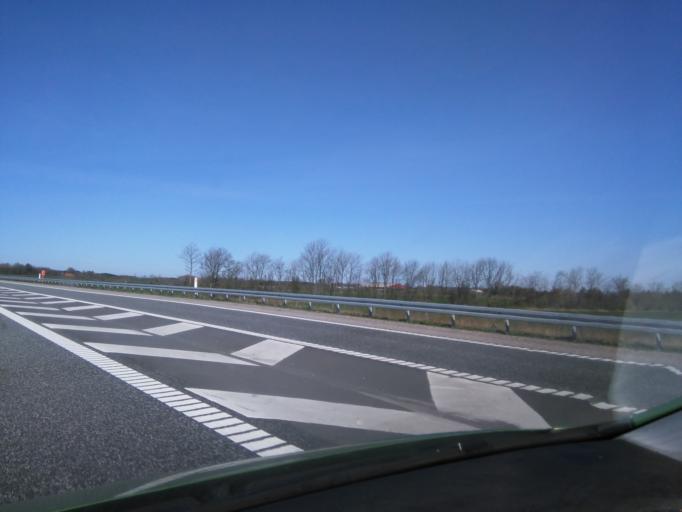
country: DK
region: South Denmark
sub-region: Vejle Kommune
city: Jelling
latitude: 55.8364
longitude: 9.3917
